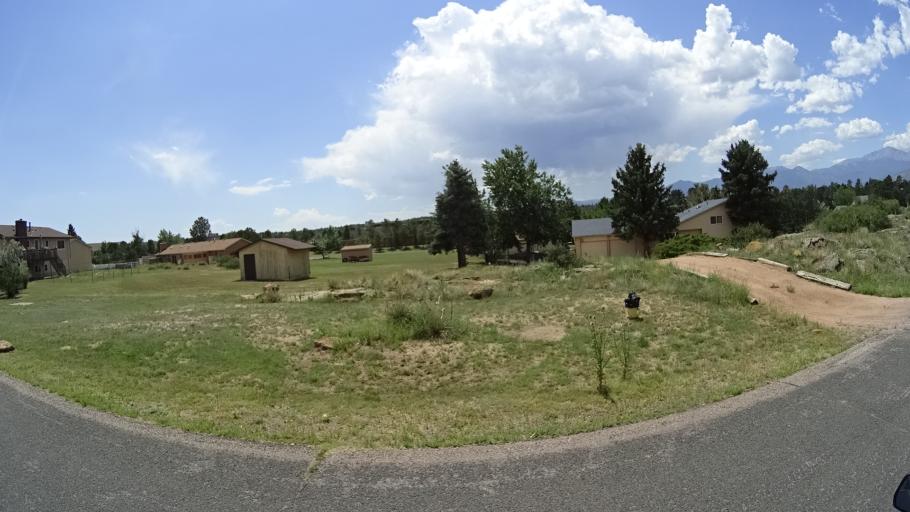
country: US
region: Colorado
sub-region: El Paso County
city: Air Force Academy
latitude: 38.9358
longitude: -104.8012
